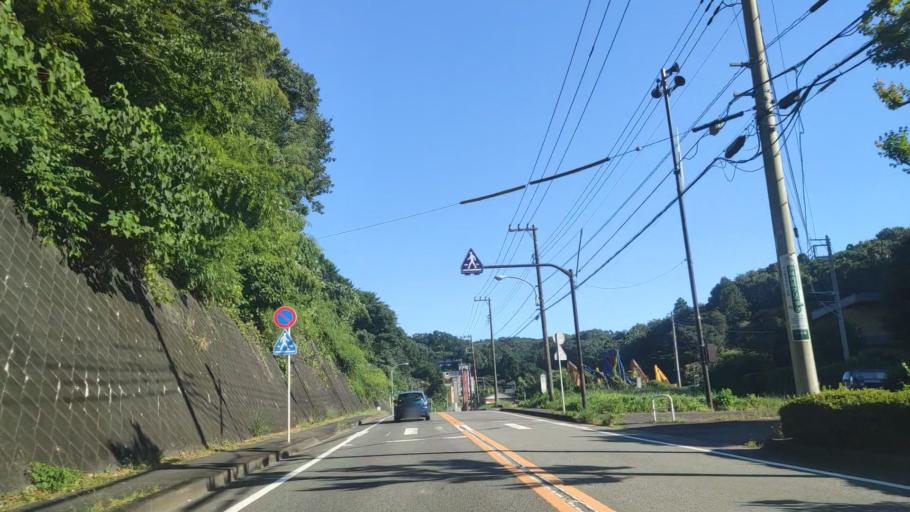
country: JP
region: Tokyo
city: Hachioji
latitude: 35.6196
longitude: 139.3146
